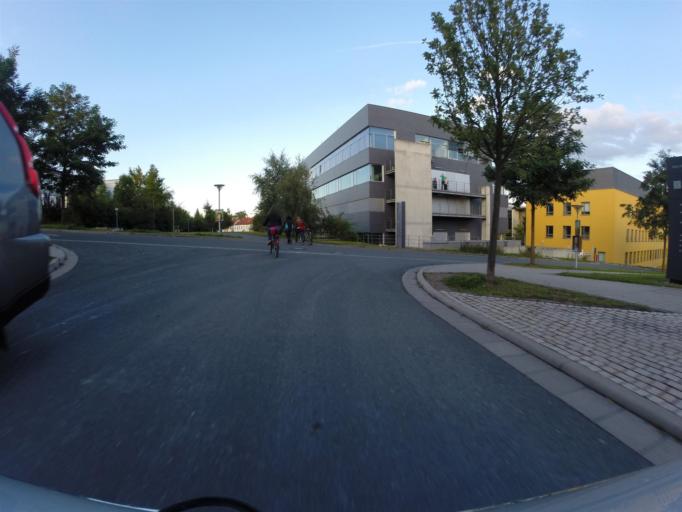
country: DE
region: Thuringia
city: Jena
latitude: 50.9099
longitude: 11.5695
